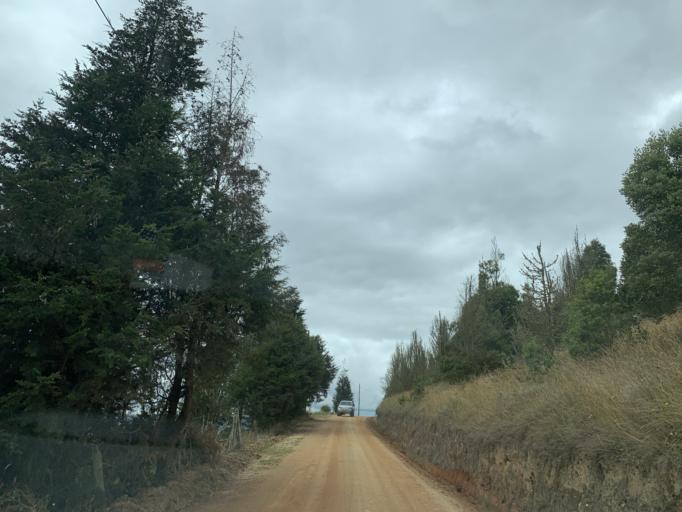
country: CO
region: Boyaca
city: Tunja
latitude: 5.5412
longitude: -73.3207
